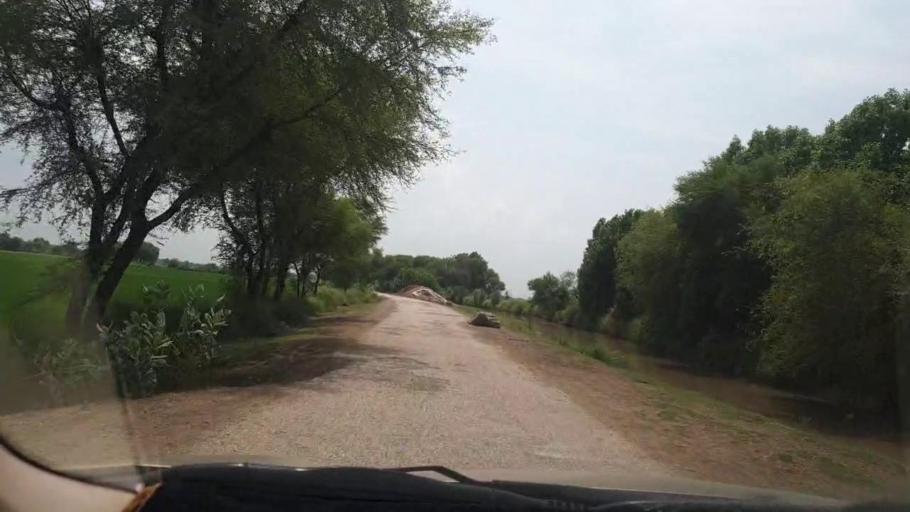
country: PK
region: Sindh
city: Larkana
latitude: 27.5989
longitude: 68.1241
